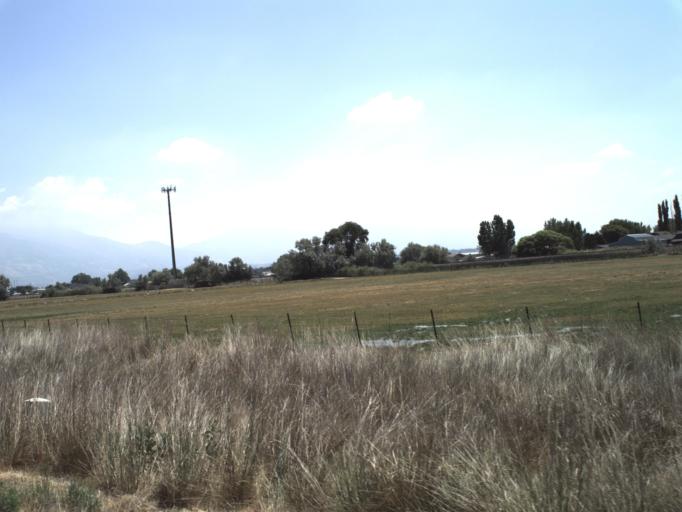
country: US
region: Utah
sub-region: Weber County
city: Plain City
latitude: 41.2459
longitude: -112.0941
